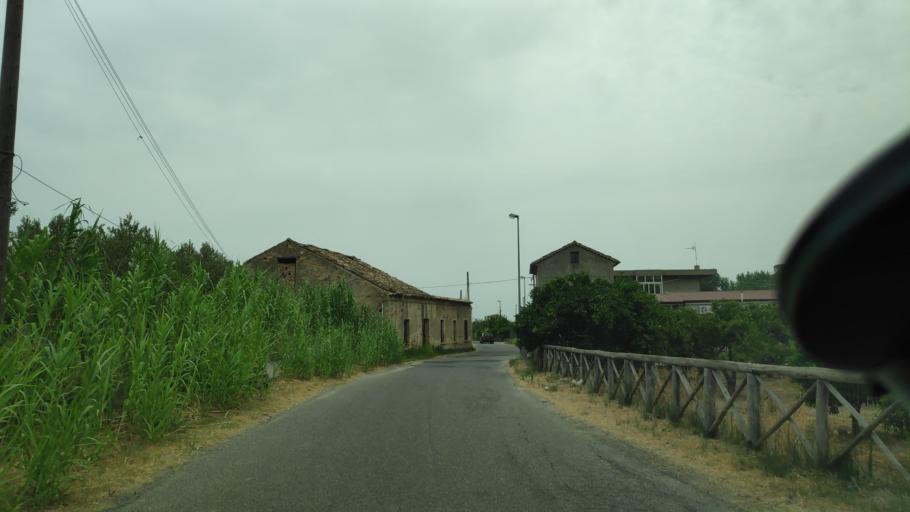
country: IT
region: Calabria
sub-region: Provincia di Catanzaro
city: Marina di Davoli
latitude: 38.6624
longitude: 16.5369
